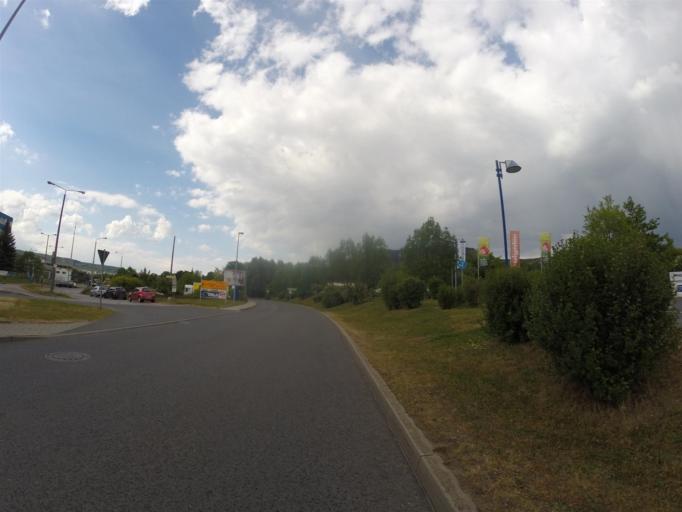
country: DE
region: Thuringia
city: Jena
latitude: 50.8996
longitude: 11.5935
